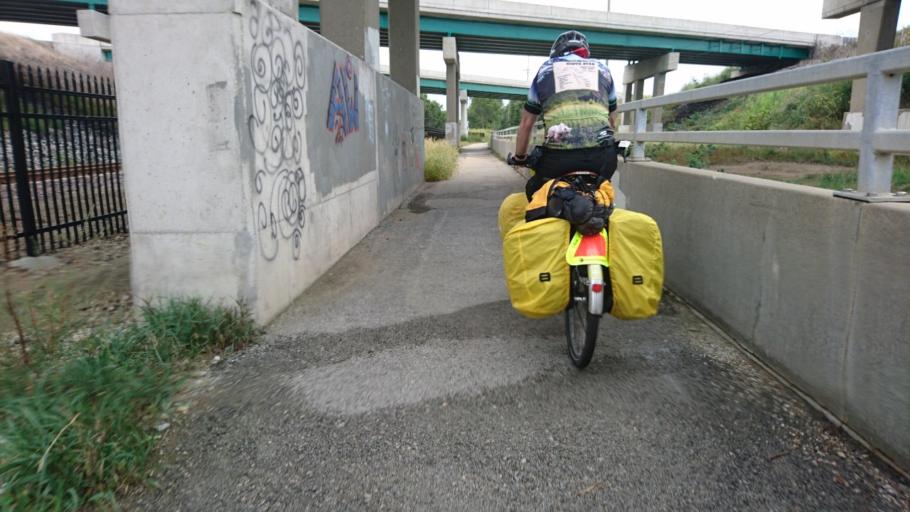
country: US
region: Illinois
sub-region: Sangamon County
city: Southern View
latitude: 39.7410
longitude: -89.6679
